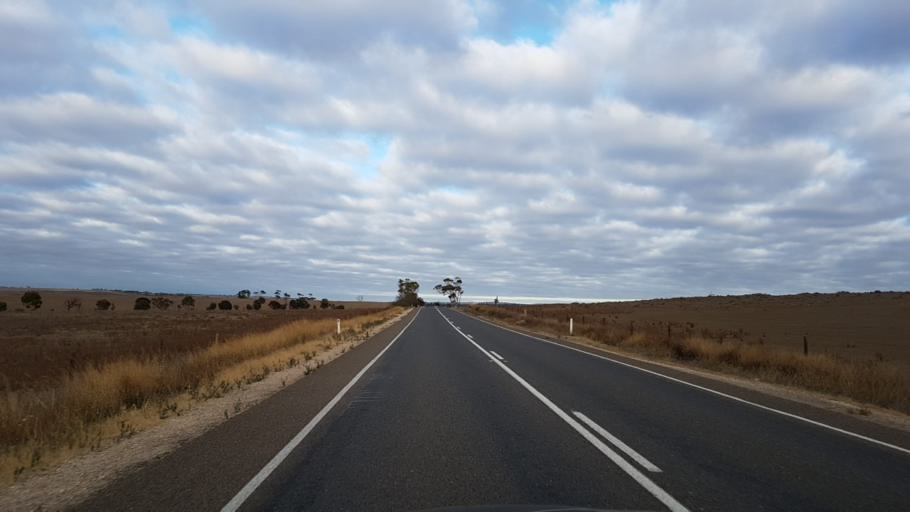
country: AU
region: South Australia
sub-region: Mount Barker
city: Callington
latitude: -35.1941
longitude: 138.9869
